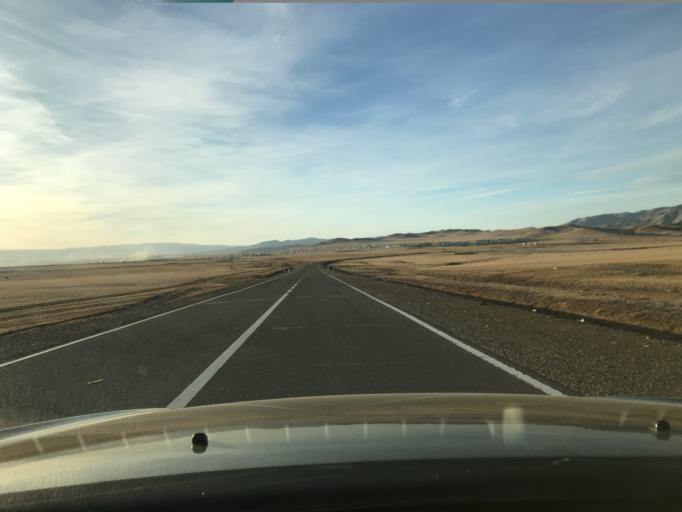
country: MN
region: Central Aimak
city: Arhust
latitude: 47.7662
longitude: 107.4252
